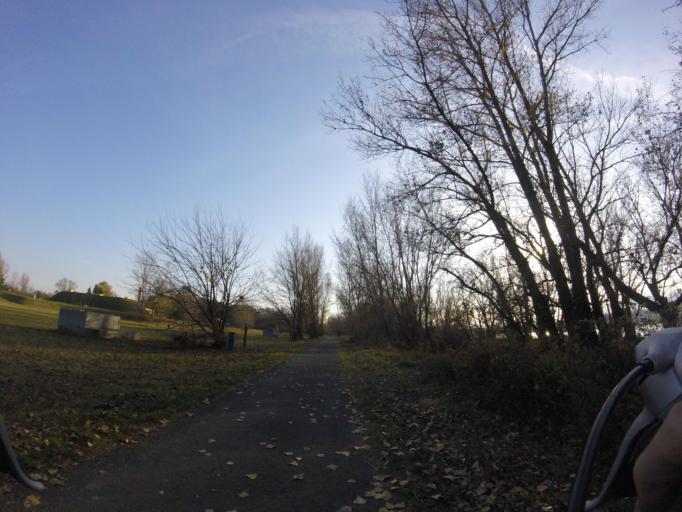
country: HU
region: Pest
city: Szodliget
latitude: 47.7378
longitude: 19.1354
